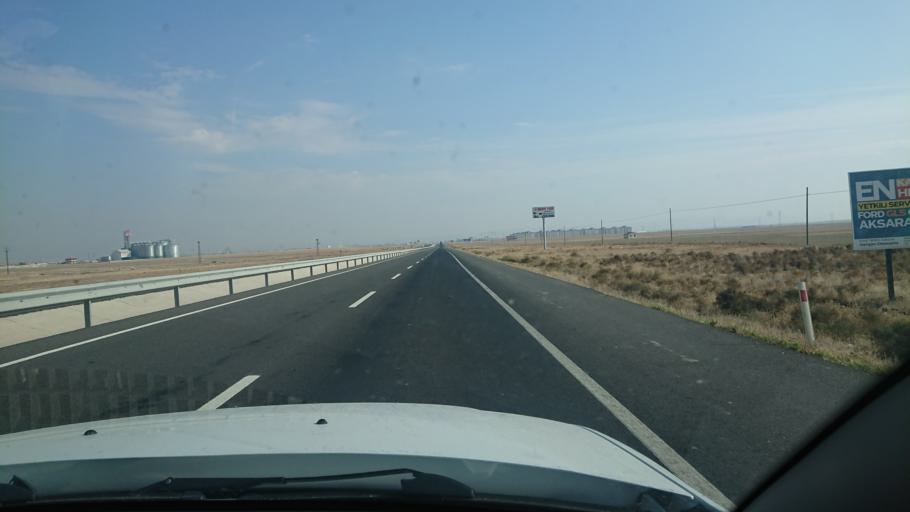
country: TR
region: Aksaray
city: Yesilova
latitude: 38.3291
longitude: 33.9011
